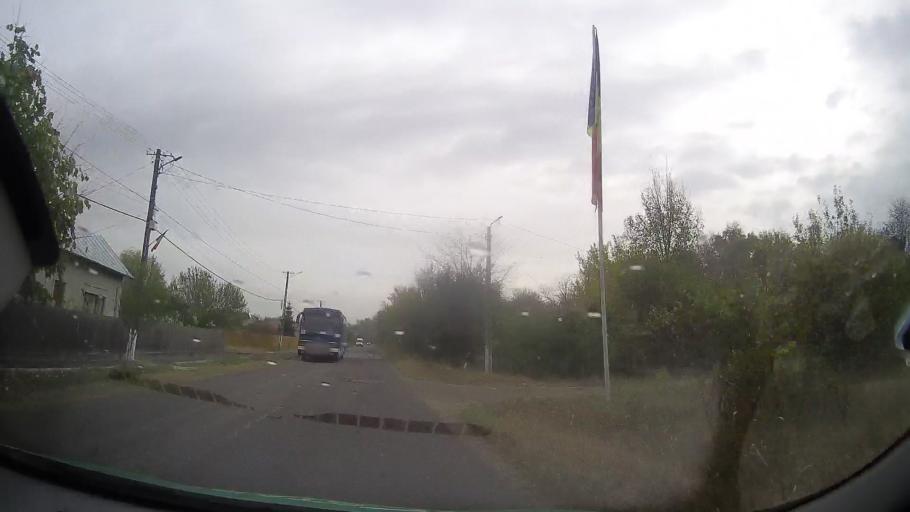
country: RO
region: Prahova
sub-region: Comuna Dumbrava
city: Dumbrava
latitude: 44.8641
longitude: 26.2037
